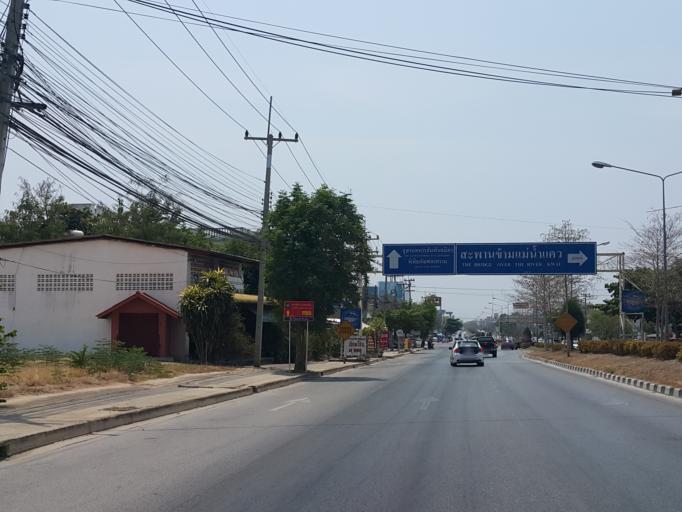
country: TH
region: Kanchanaburi
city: Kanchanaburi
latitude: 14.0476
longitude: 99.5080
